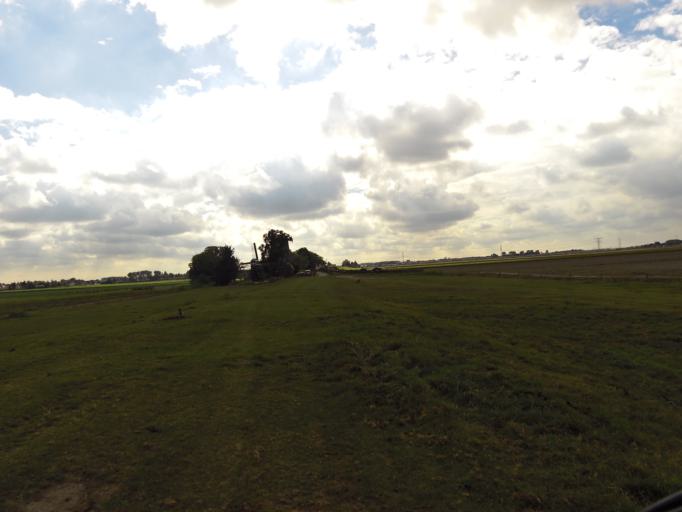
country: NL
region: South Holland
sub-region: Gemeente Rijnwoude
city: Benthuizen
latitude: 52.0522
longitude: 4.5640
